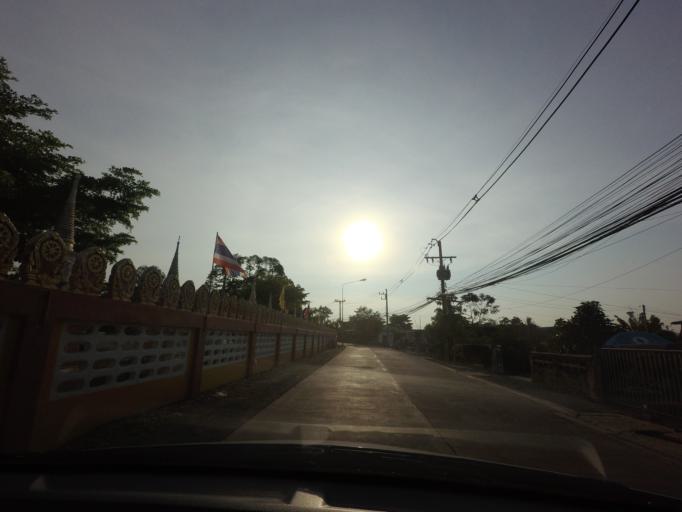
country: TH
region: Pathum Thani
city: Pathum Thani
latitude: 14.0373
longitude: 100.5463
